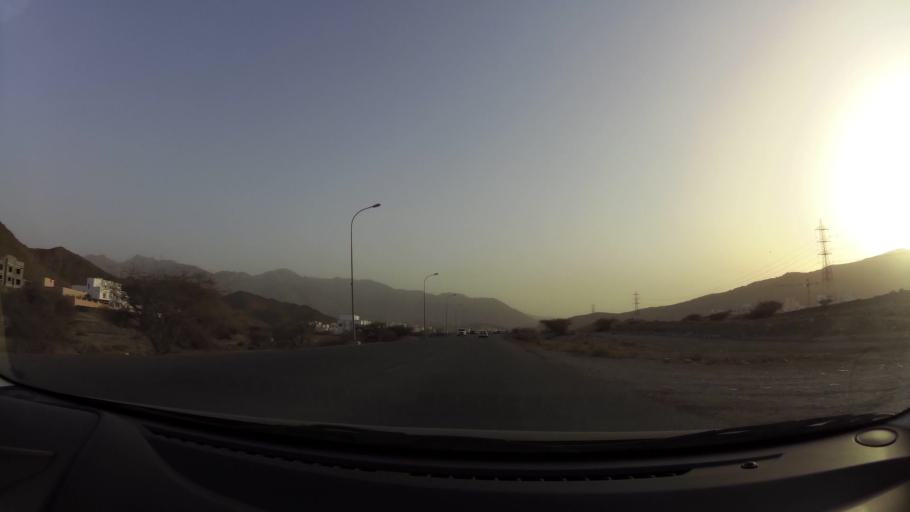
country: OM
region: Muhafazat Masqat
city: Bawshar
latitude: 23.4933
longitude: 58.3207
